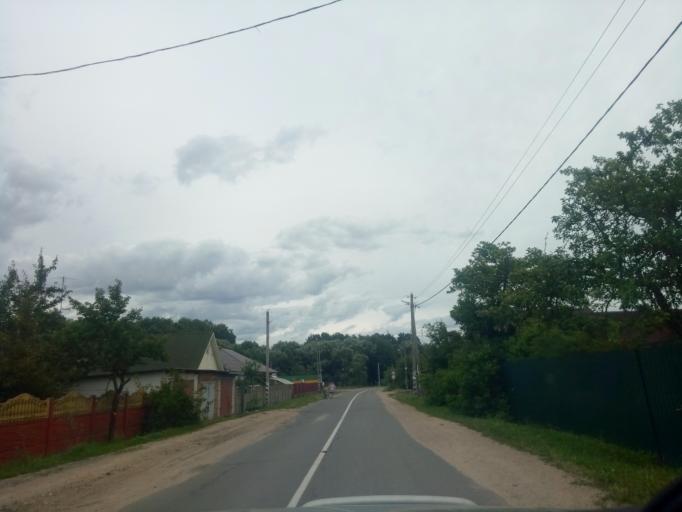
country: BY
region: Minsk
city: Zhdanovichy
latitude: 53.9297
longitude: 27.3819
